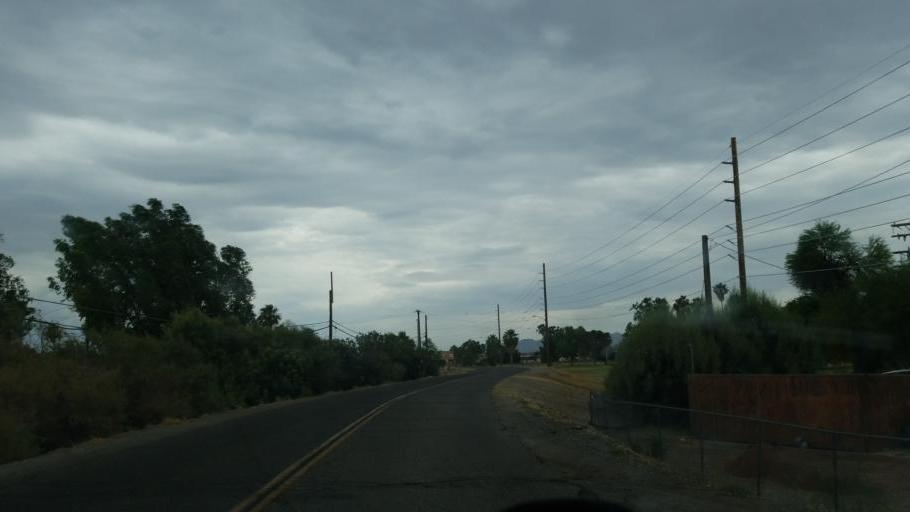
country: US
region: California
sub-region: San Bernardino County
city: Needles
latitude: 34.8473
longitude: -114.6071
